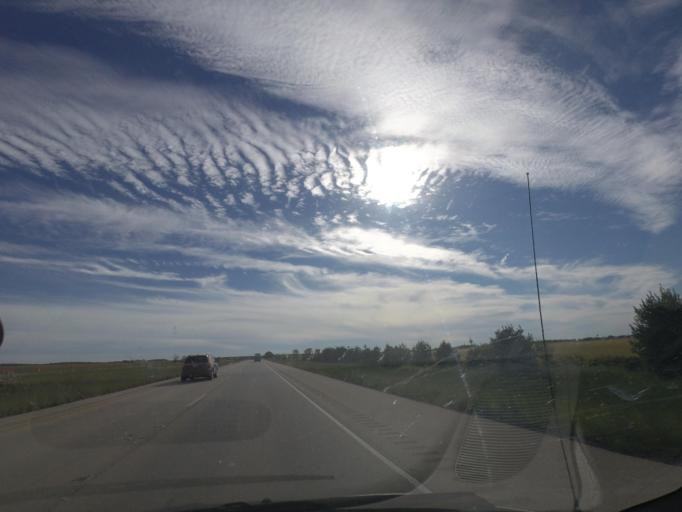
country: US
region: Illinois
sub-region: Piatt County
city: Cerro Gordo
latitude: 39.9428
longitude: -88.8333
